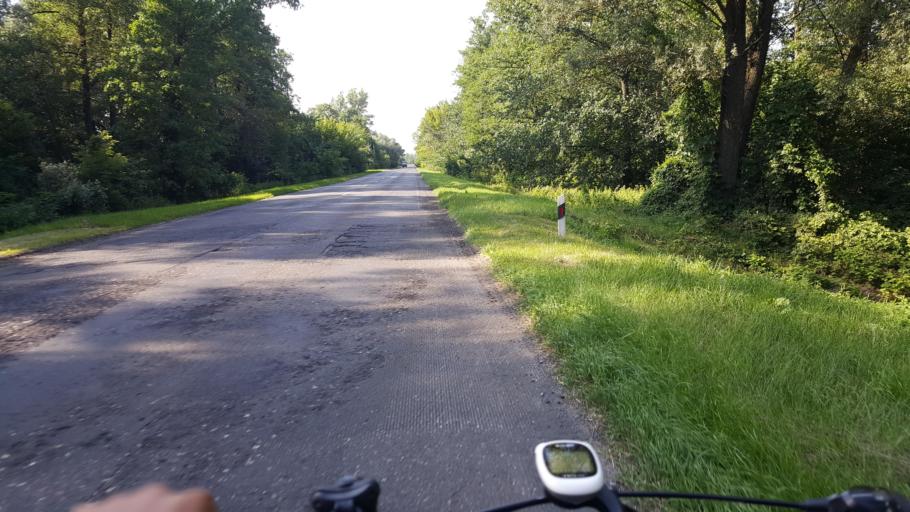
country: BY
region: Brest
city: Zhabinka
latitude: 52.2908
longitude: 23.9412
